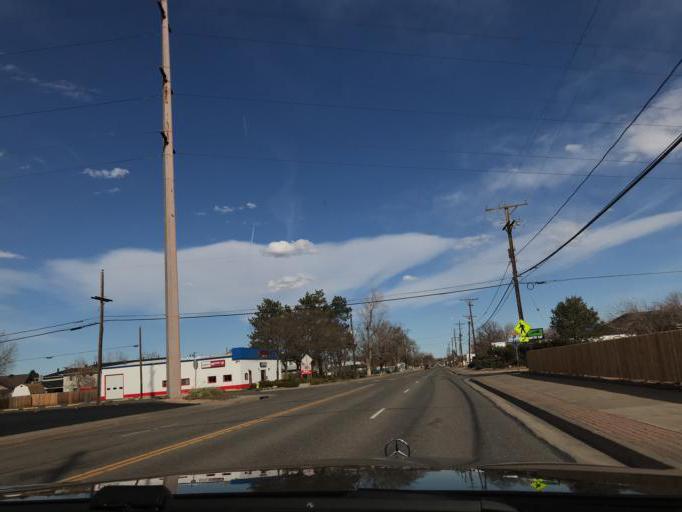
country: US
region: Colorado
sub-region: Jefferson County
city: Arvada
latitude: 39.7781
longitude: -105.1218
